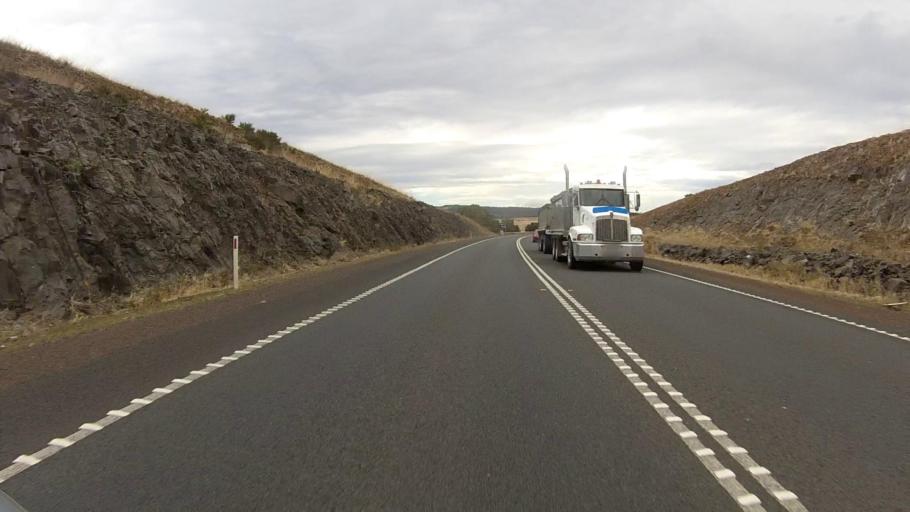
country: AU
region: Tasmania
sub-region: Brighton
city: Bridgewater
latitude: -42.3237
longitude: 147.3445
